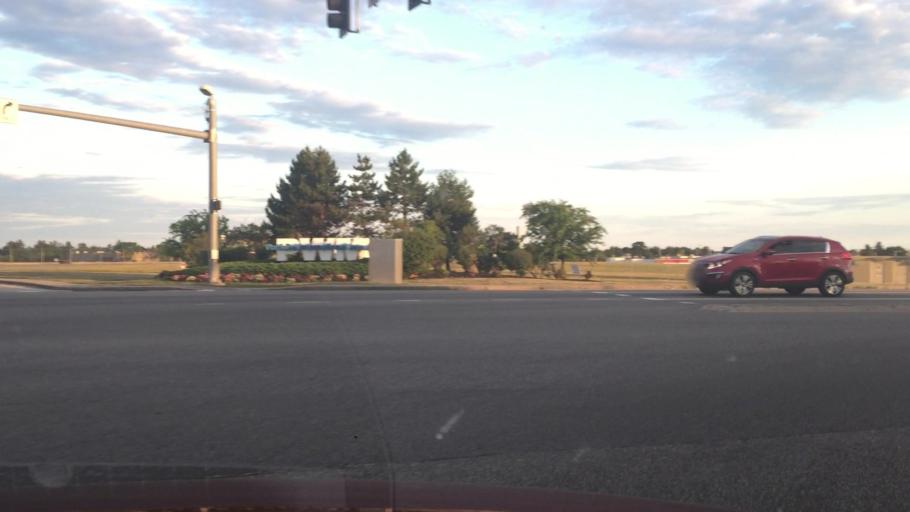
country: US
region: Maine
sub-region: Cumberland County
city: South Portland Gardens
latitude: 43.6482
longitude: -70.3270
